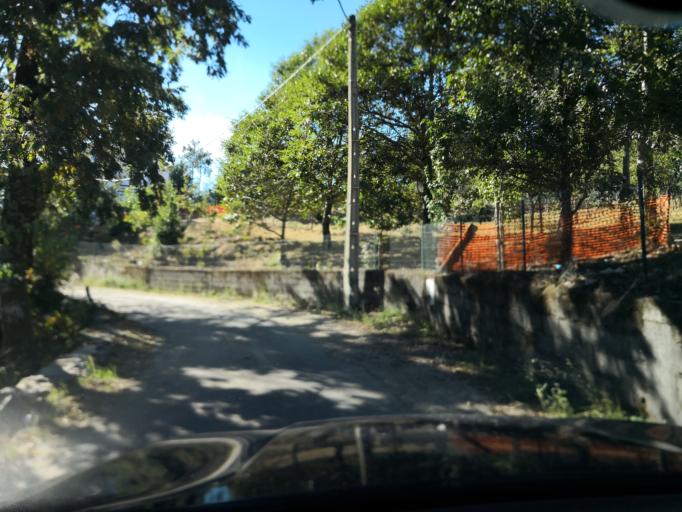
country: PT
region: Vila Real
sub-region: Santa Marta de Penaguiao
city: Santa Marta de Penaguiao
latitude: 41.2949
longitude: -7.8612
